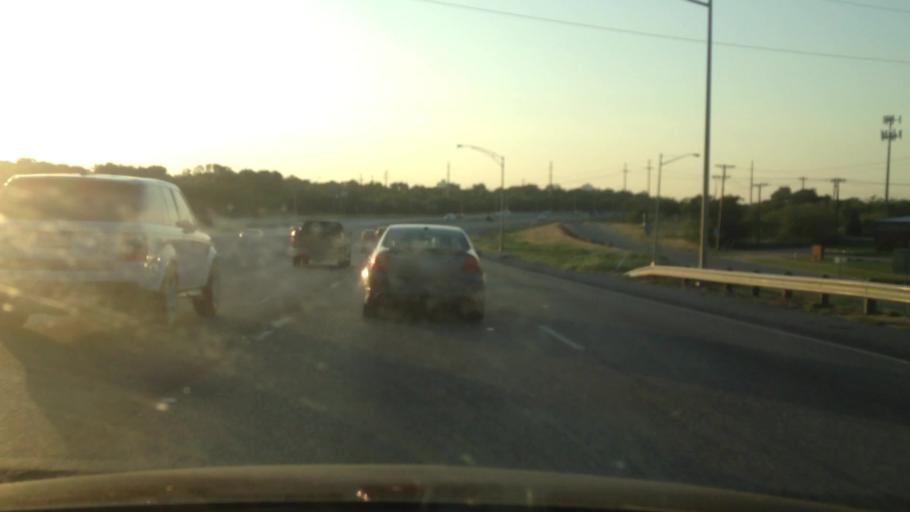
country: US
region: Texas
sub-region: Tarrant County
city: Fort Worth
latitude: 32.7231
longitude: -97.2947
